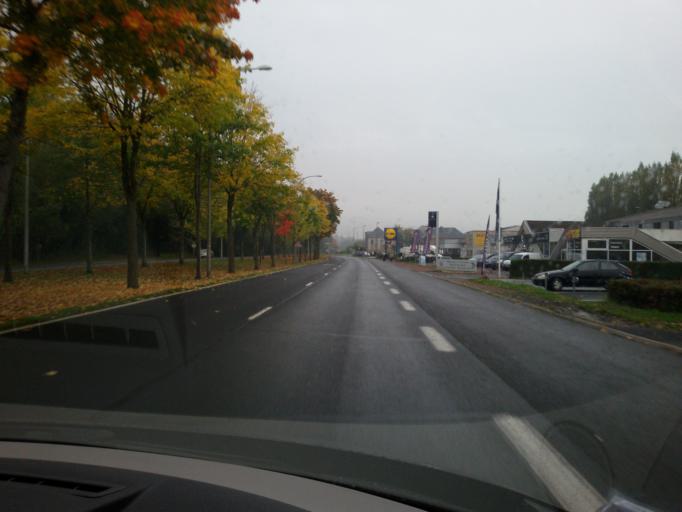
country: FR
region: Lower Normandy
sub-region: Departement du Calvados
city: Honfleur
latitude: 49.4146
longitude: 0.2468
